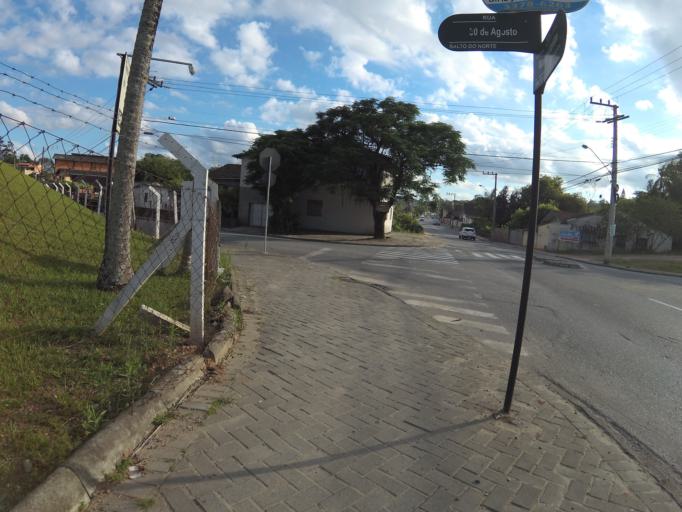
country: BR
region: Santa Catarina
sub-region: Blumenau
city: Blumenau
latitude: -26.8721
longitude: -49.0958
